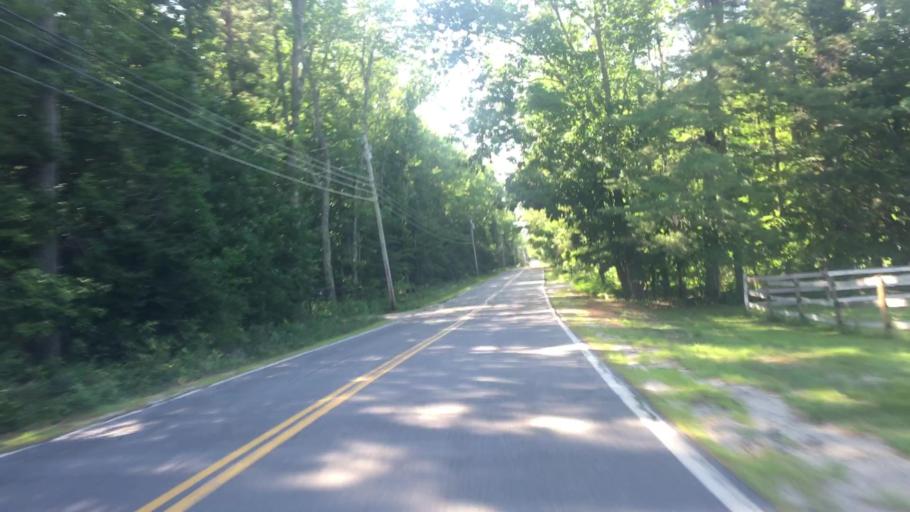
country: US
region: Maine
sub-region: York County
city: Hollis Center
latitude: 43.6350
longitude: -70.5740
